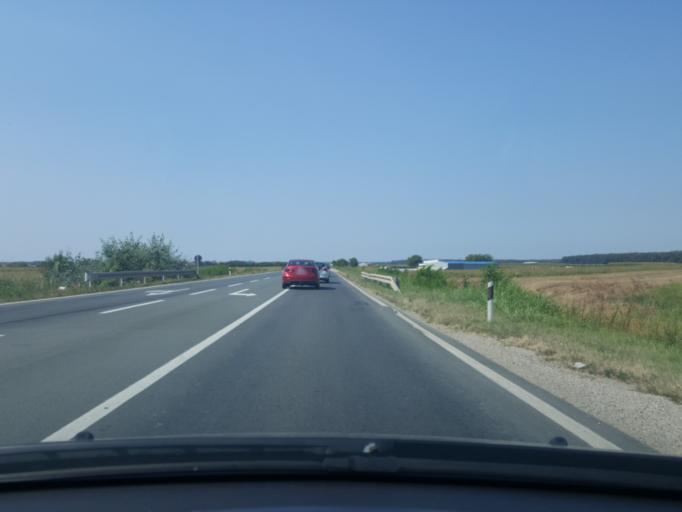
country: RS
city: Klenak
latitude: 44.7747
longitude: 19.7253
